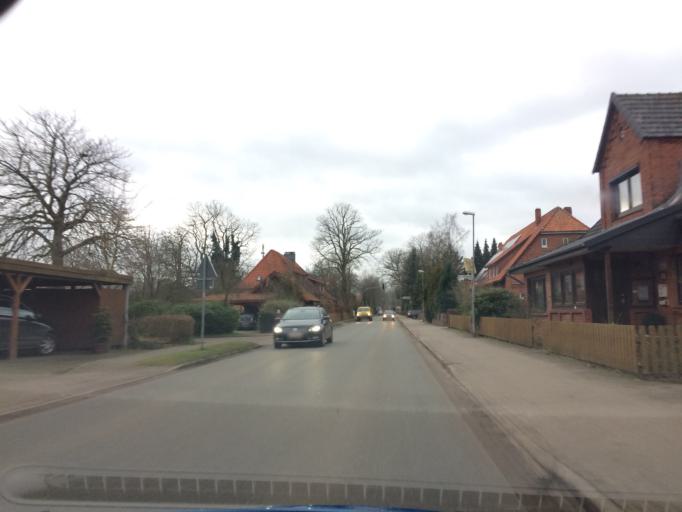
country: DE
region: Lower Saxony
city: Radbruch
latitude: 53.3098
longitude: 10.2893
